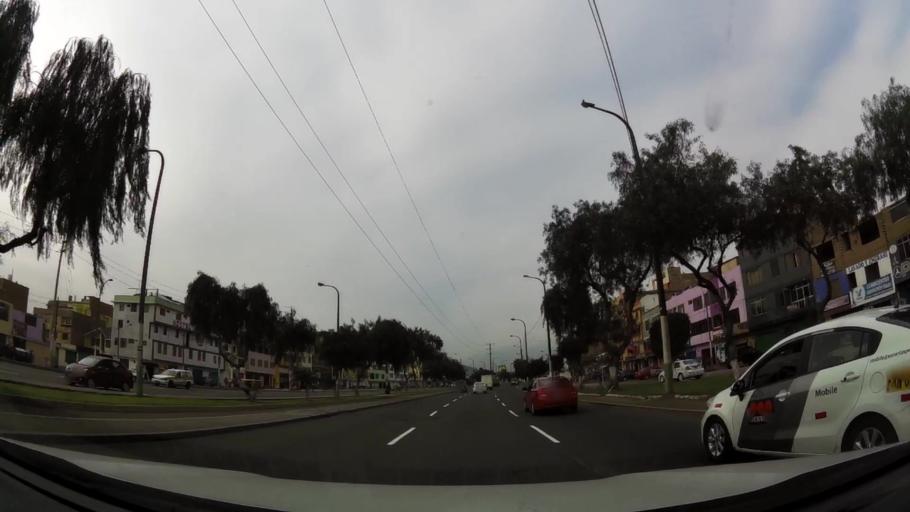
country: PE
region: Callao
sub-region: Callao
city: Callao
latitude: -12.0127
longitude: -77.0936
